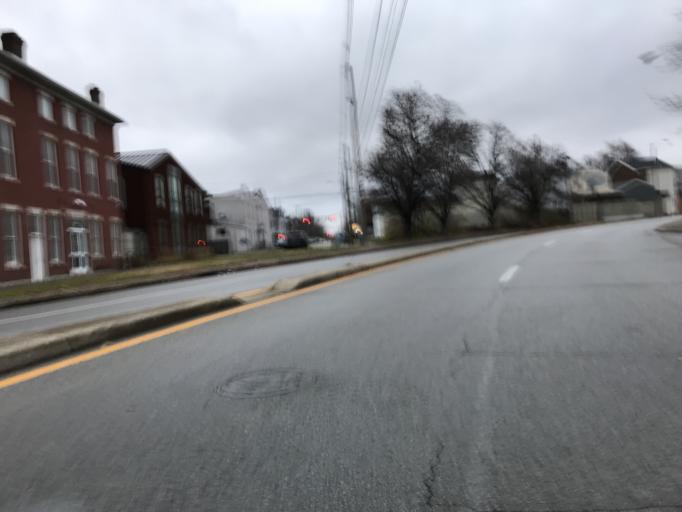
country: US
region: Kentucky
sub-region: Jefferson County
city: Louisville
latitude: 38.2457
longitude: -85.7372
